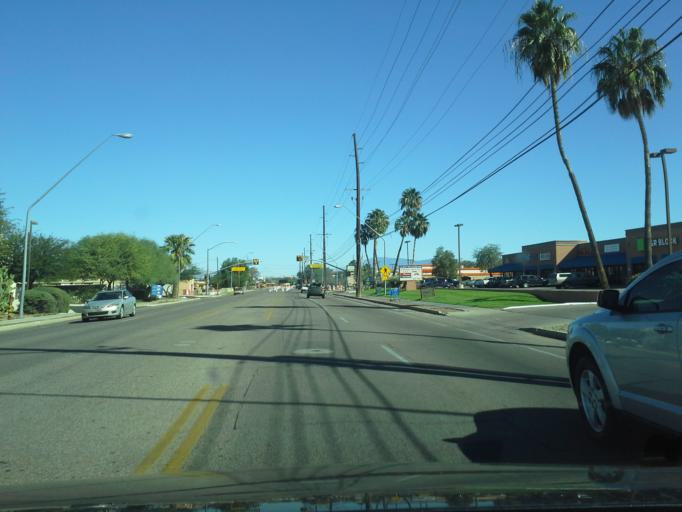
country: US
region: Arizona
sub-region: Pima County
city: South Tucson
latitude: 32.2292
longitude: -110.9937
